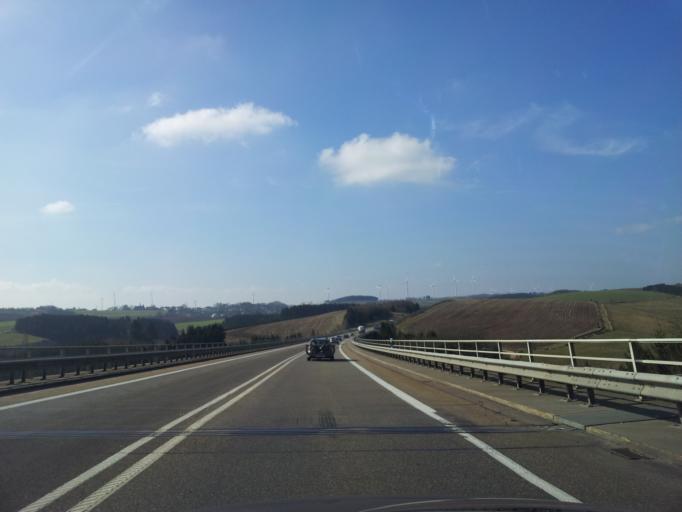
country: DE
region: Rheinland-Pfalz
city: Habscheid
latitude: 50.2010
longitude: 6.2858
